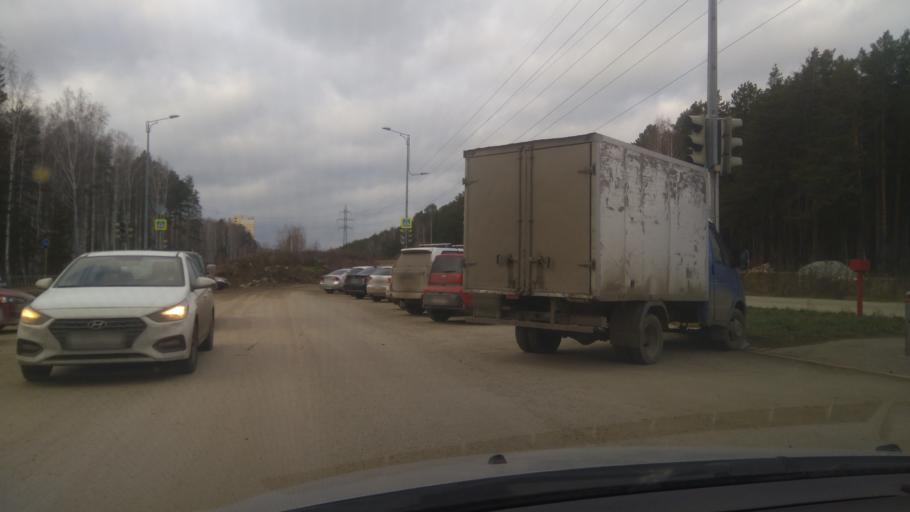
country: RU
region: Sverdlovsk
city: Sovkhoznyy
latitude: 56.7870
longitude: 60.5469
